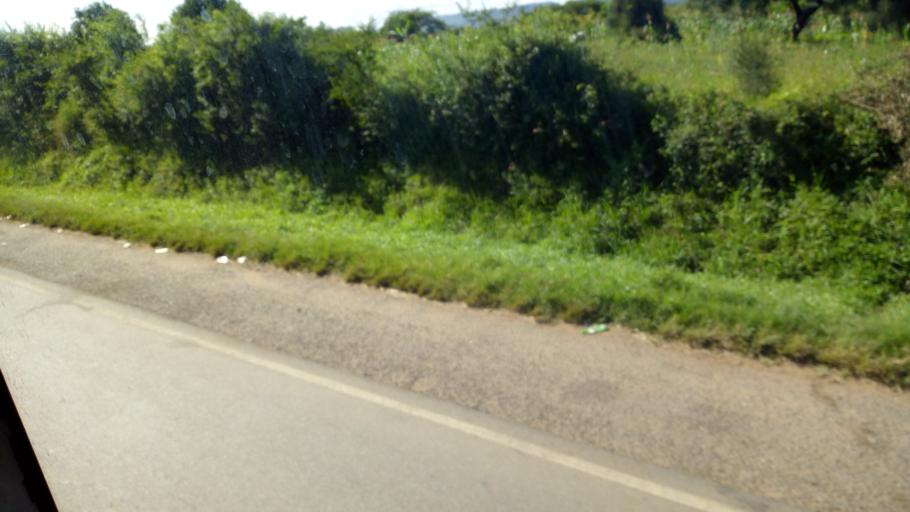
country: UG
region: Central Region
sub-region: Lyantonde District
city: Lyantonde
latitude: -0.4180
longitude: 31.1201
